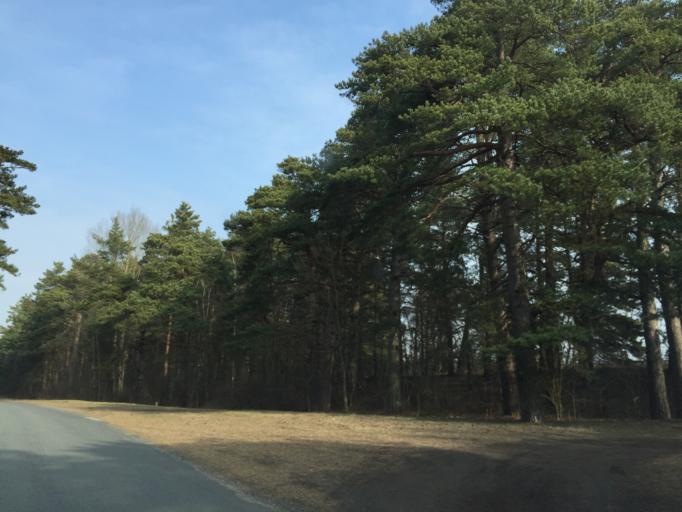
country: LV
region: Salacgrivas
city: Ainazi
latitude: 57.8825
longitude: 24.3658
